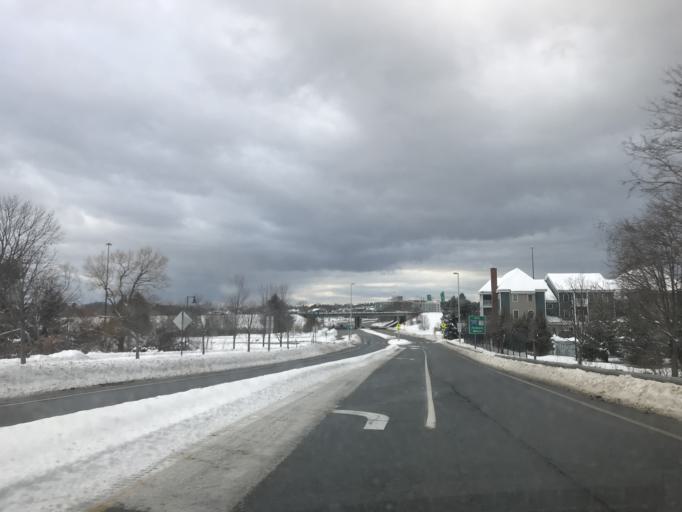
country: US
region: Maine
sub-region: Cumberland County
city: Portland
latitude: 43.6515
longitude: -70.2848
